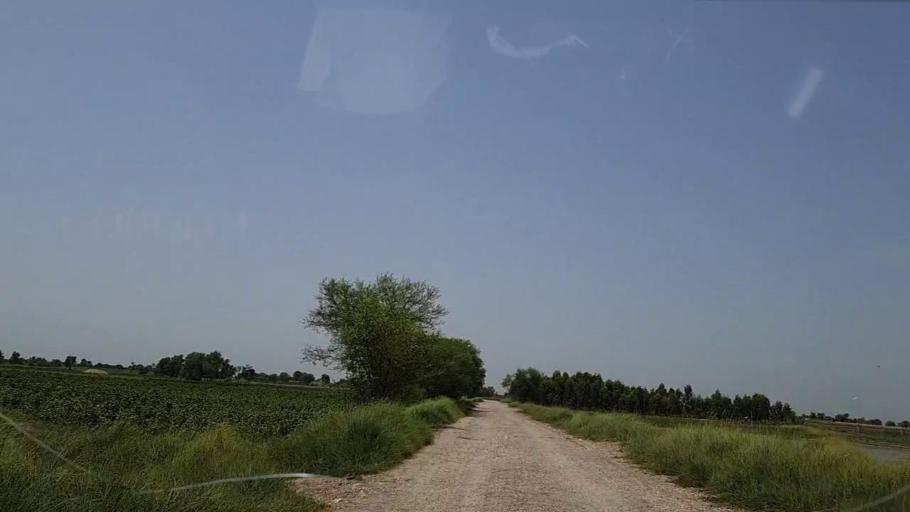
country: PK
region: Sindh
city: Tharu Shah
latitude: 26.9357
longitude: 68.0477
